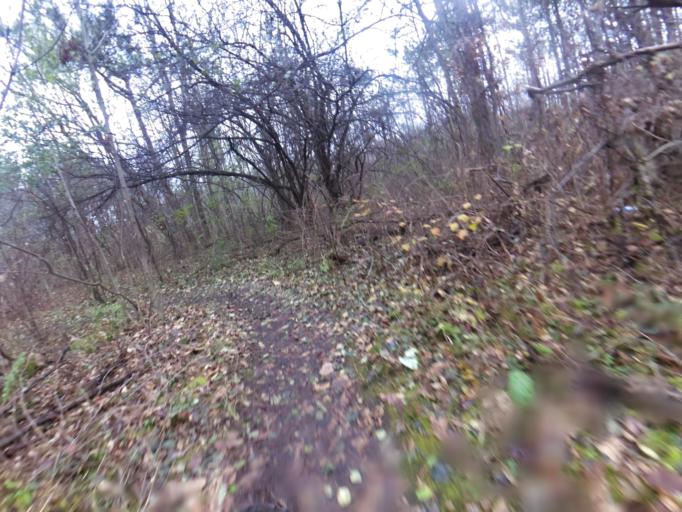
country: CA
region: Ontario
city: Bells Corners
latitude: 45.2877
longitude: -75.8338
